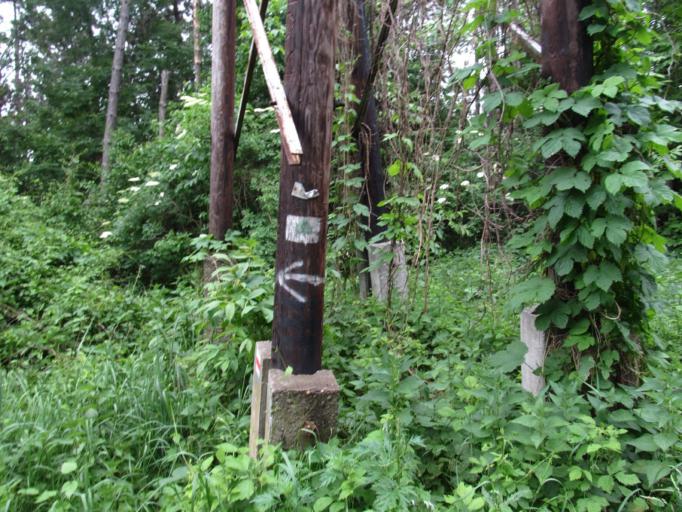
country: HU
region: Borsod-Abauj-Zemplen
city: Tokaj
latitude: 48.1228
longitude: 21.3950
